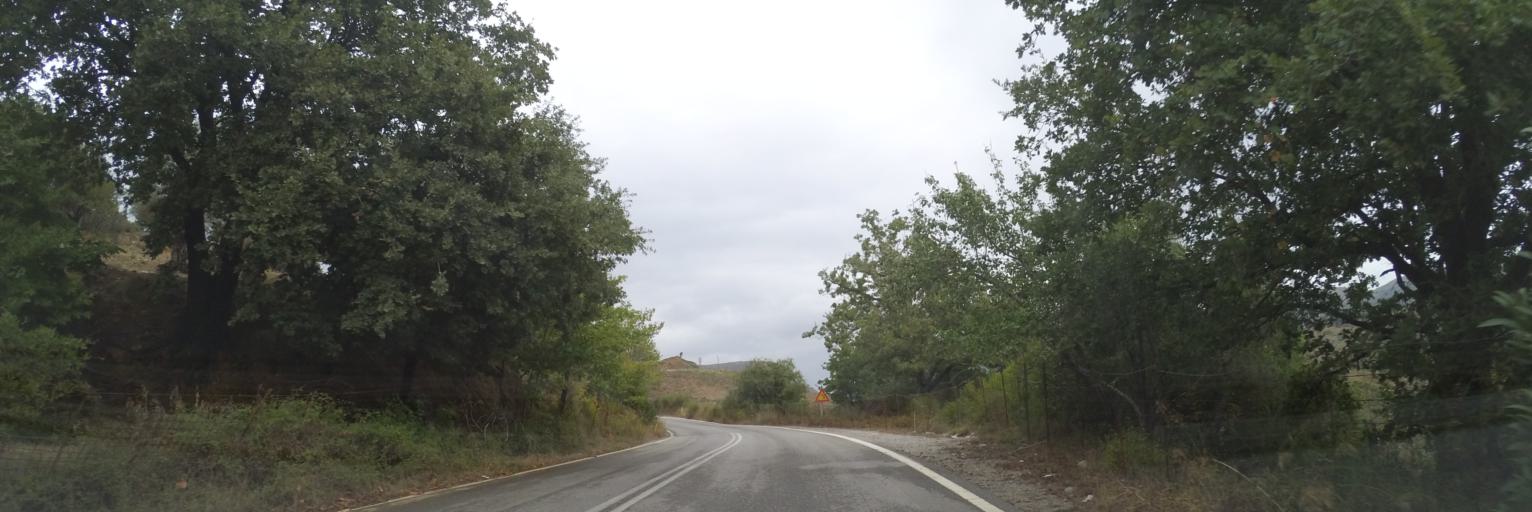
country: GR
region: Crete
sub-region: Nomos Rethymnis
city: Agia Foteini
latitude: 35.2908
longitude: 24.5633
